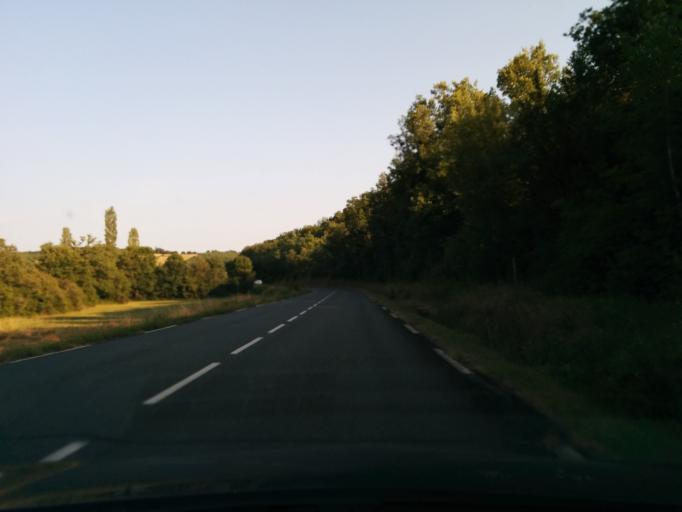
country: FR
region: Midi-Pyrenees
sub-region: Departement du Lot
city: Le Vigan
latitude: 44.6971
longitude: 1.4808
